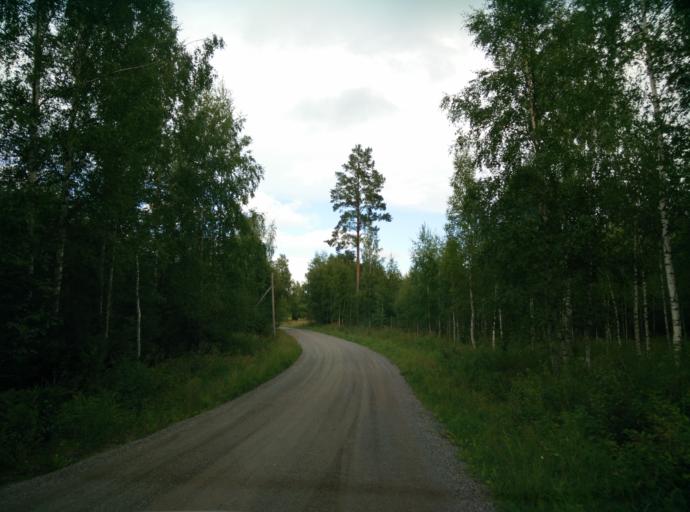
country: FI
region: Haeme
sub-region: Haemeenlinna
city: Kalvola
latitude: 61.1168
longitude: 24.1393
